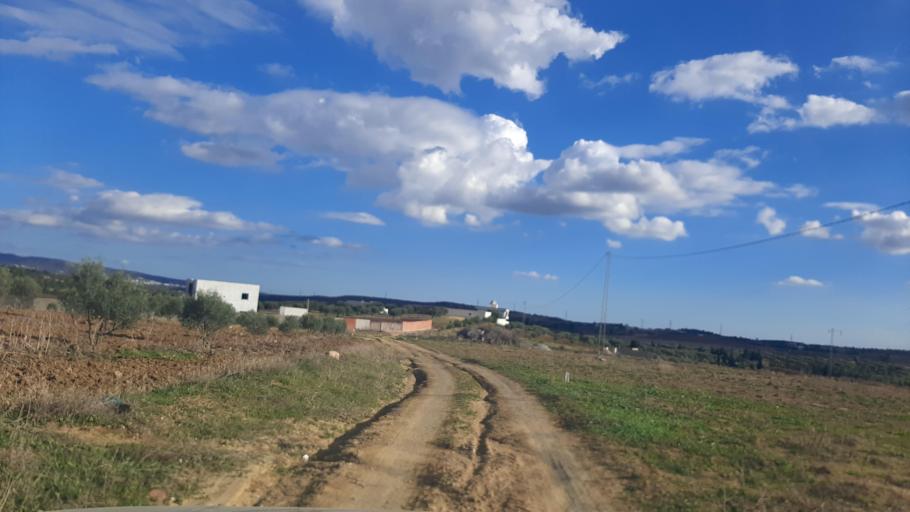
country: TN
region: Nabul
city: Bu `Urqub
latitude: 36.4554
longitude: 10.4979
